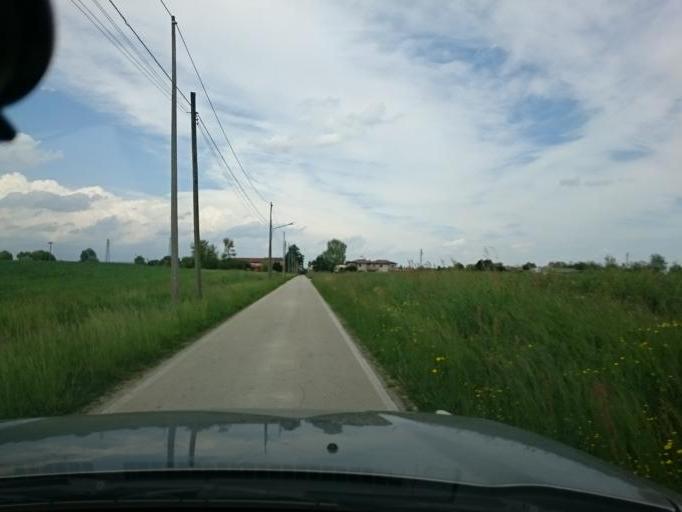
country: IT
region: Veneto
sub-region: Provincia di Vicenza
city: Torri di Quartesolo
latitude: 45.5059
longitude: 11.5987
